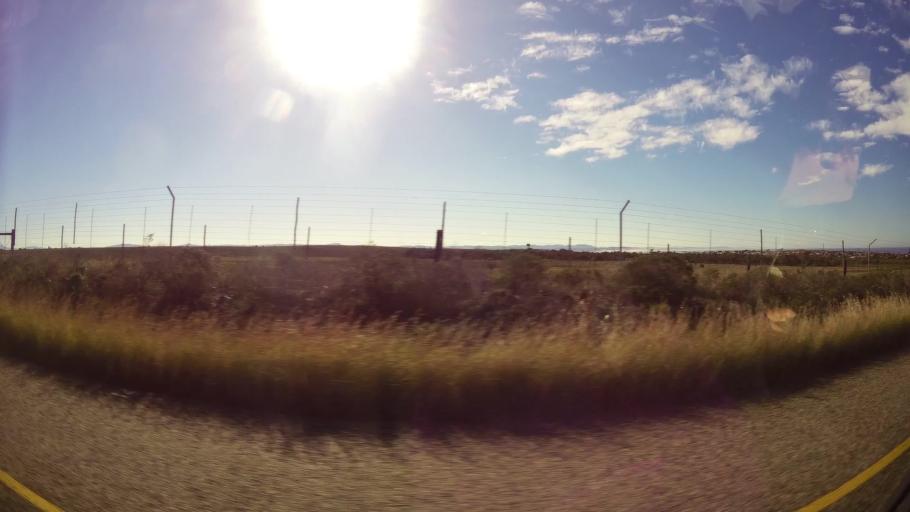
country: ZA
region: Eastern Cape
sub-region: Cacadu District Municipality
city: Jeffrey's Bay
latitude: -34.0227
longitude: 24.8950
